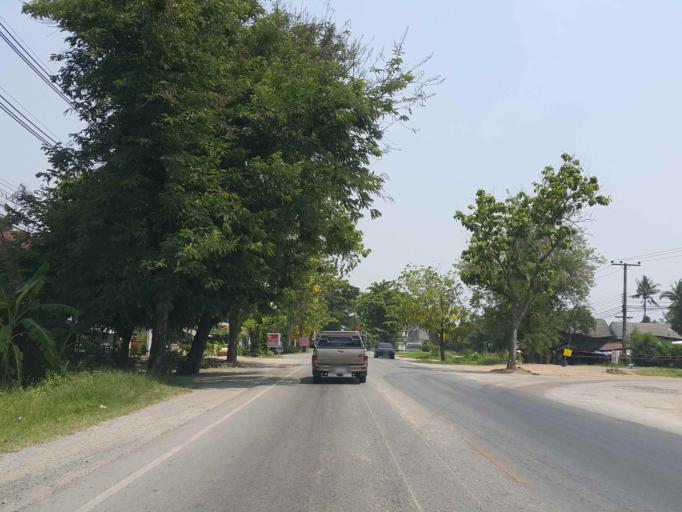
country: TH
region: Chiang Mai
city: San Sai
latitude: 18.9676
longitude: 98.9835
